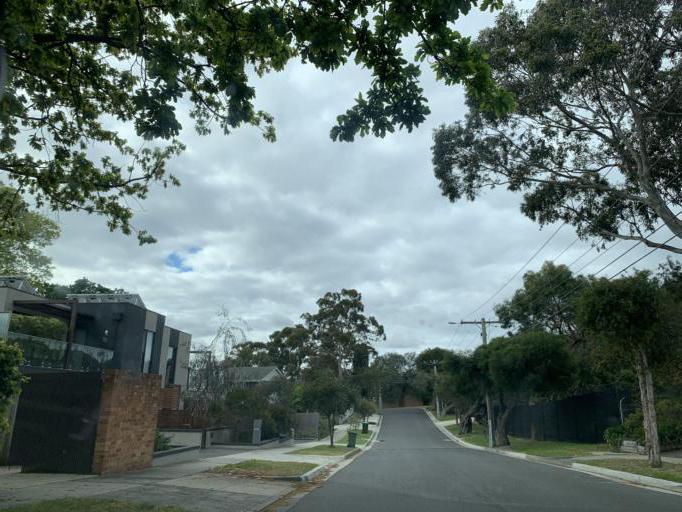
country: AU
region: Victoria
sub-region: Bayside
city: Cheltenham
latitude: -37.9696
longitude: 145.0426
